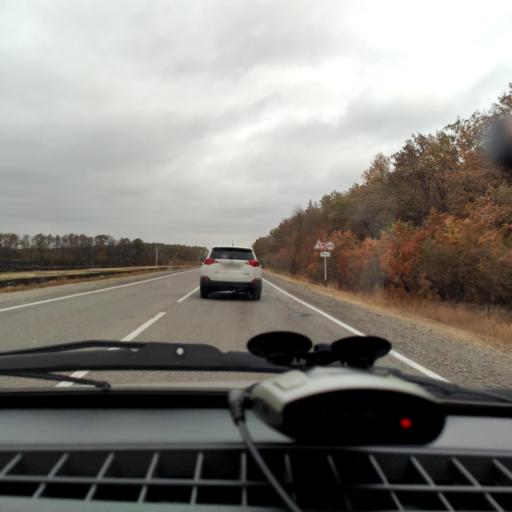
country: RU
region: Voronezj
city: Shilovo
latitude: 51.4232
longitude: 39.0075
